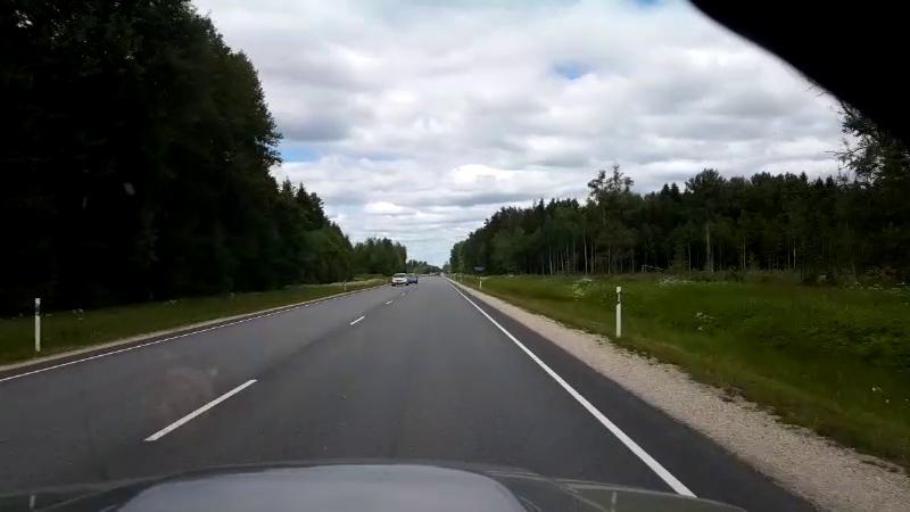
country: EE
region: Raplamaa
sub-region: Maerjamaa vald
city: Marjamaa
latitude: 58.8003
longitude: 24.4128
